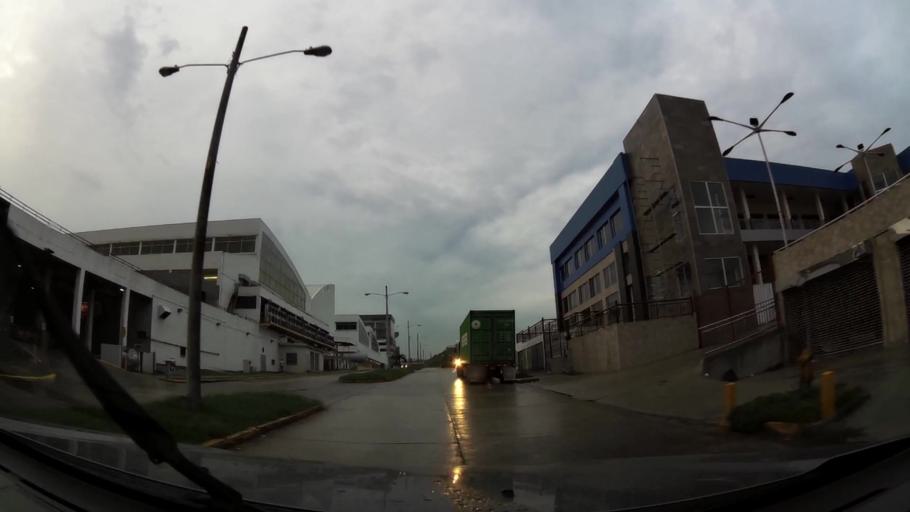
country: PA
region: Panama
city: Panama
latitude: 9.0307
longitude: -79.5306
